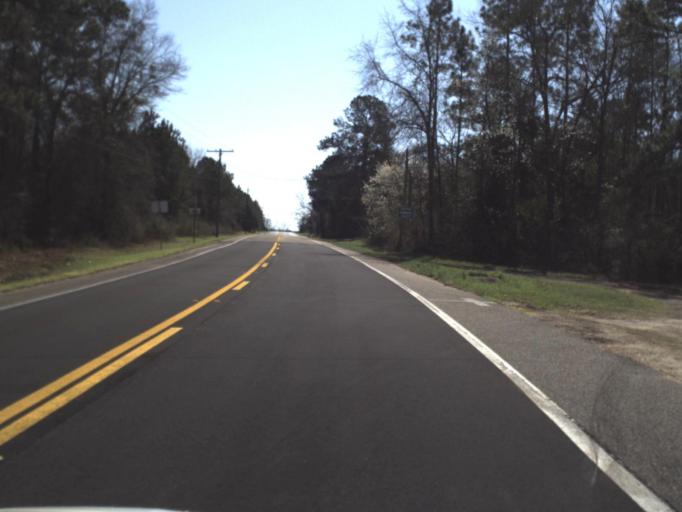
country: US
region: Florida
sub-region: Jackson County
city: Marianna
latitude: 30.6083
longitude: -85.1468
